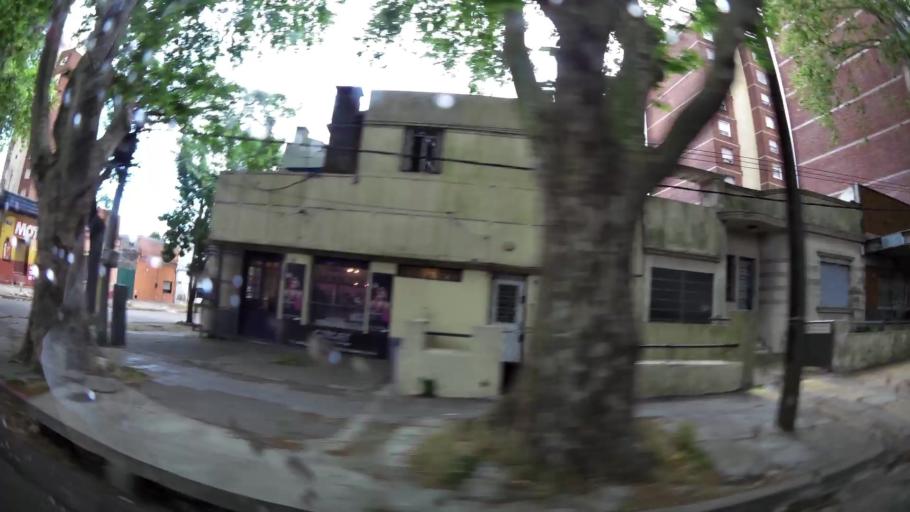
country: UY
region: Montevideo
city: Montevideo
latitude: -34.8596
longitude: -56.1772
